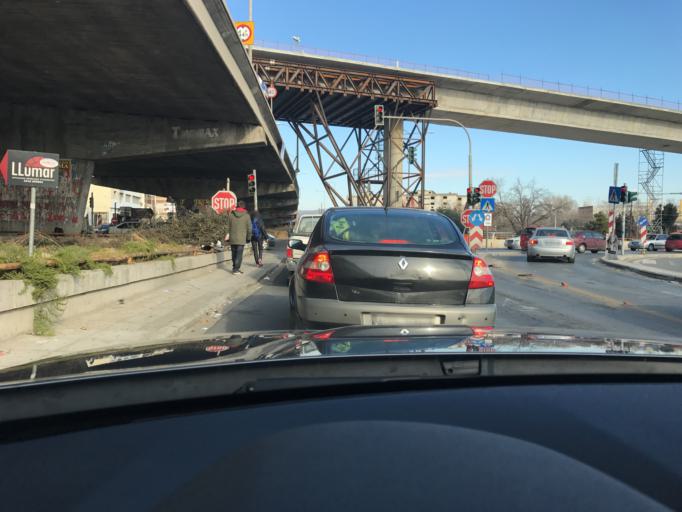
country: GR
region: Central Macedonia
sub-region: Nomos Thessalonikis
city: Stavroupoli
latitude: 40.6771
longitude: 22.9391
